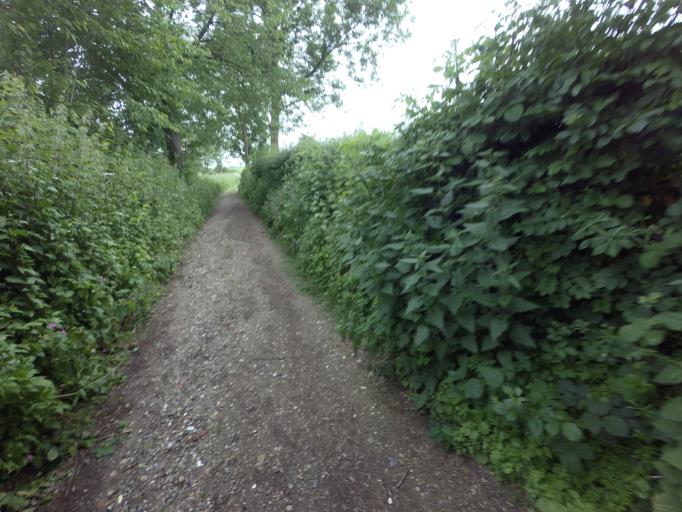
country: NL
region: Limburg
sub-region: Gemeente Voerendaal
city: Ubachsberg
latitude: 50.8546
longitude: 5.9529
